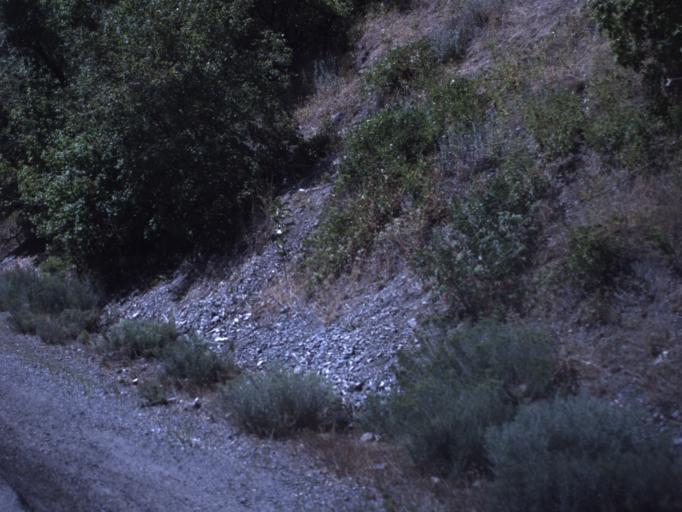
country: US
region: Utah
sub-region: Cache County
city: North Logan
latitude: 41.7426
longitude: -111.7661
